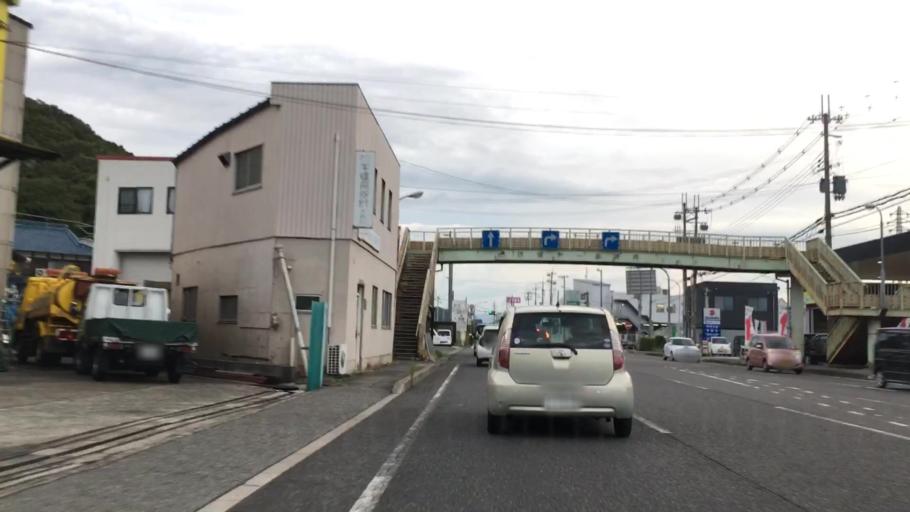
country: JP
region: Hyogo
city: Himeji
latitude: 34.8714
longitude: 134.7293
